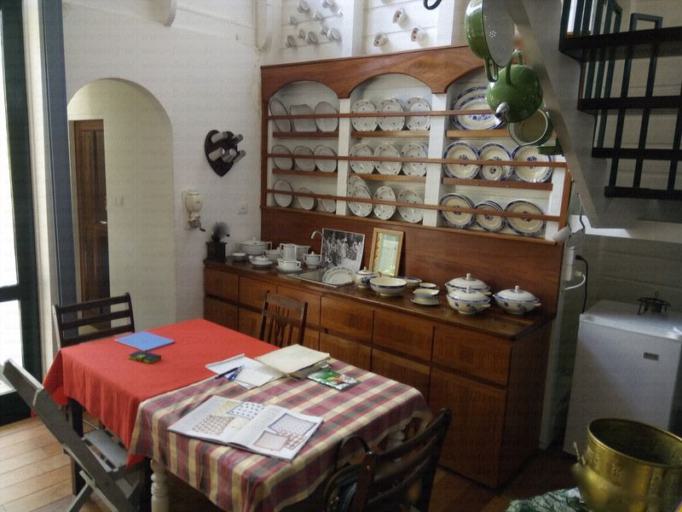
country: SR
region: Paramaribo
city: Paramaribo
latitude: 5.7684
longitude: -55.1568
